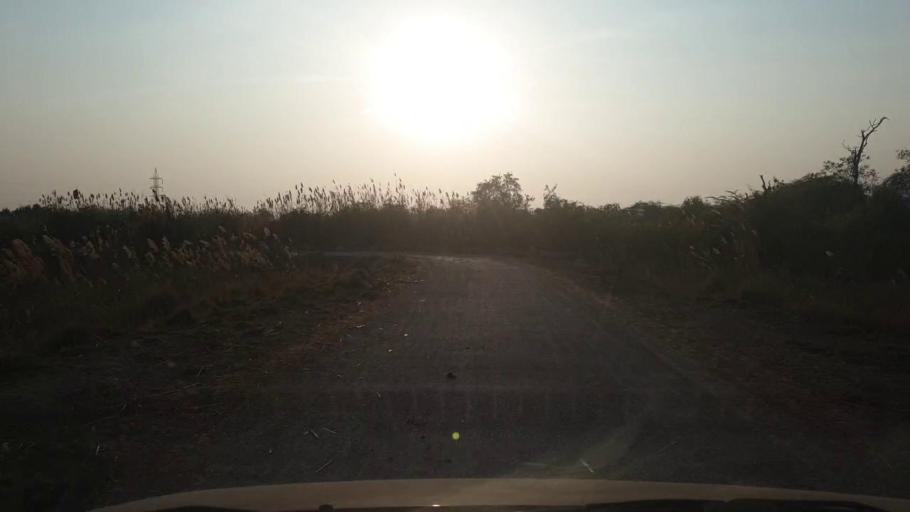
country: PK
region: Sindh
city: Mirwah Gorchani
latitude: 25.3194
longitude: 69.1560
